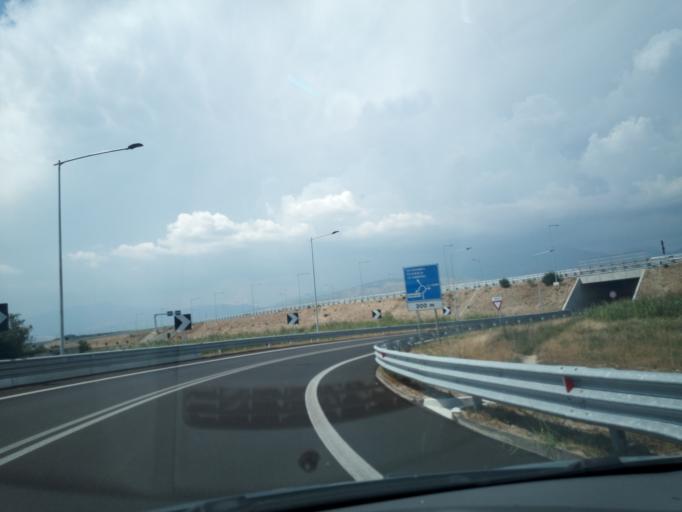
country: IT
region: Calabria
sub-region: Provincia di Cosenza
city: Doria
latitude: 39.7223
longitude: 16.3649
